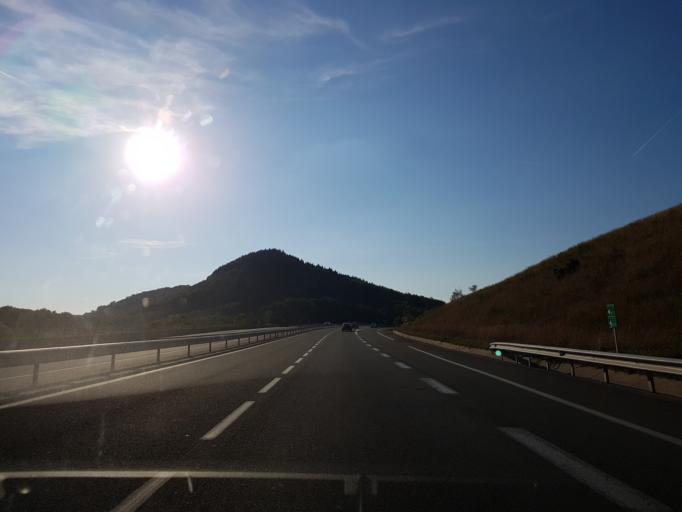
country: FR
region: Franche-Comte
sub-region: Departement de la Haute-Saone
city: Ronchamp
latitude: 47.6239
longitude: 6.6517
